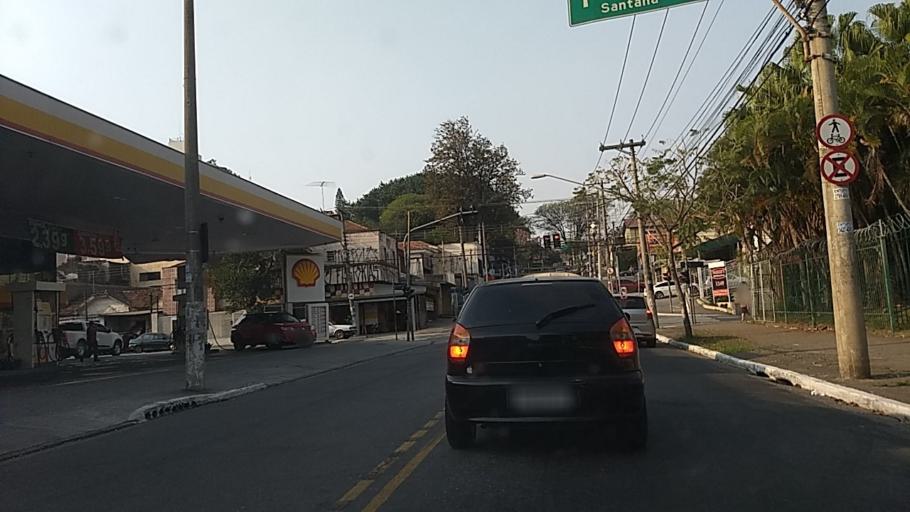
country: BR
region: Sao Paulo
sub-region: Sao Paulo
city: Sao Paulo
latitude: -23.5090
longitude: -46.6004
